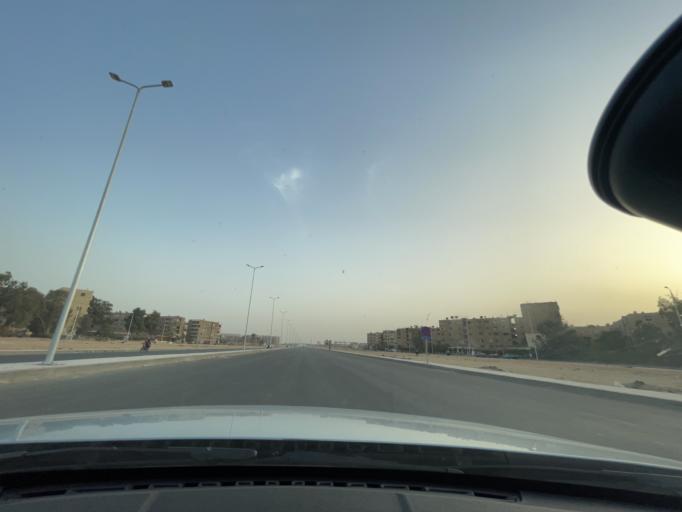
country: EG
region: Muhafazat al Qahirah
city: Cairo
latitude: 30.0456
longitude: 31.3639
